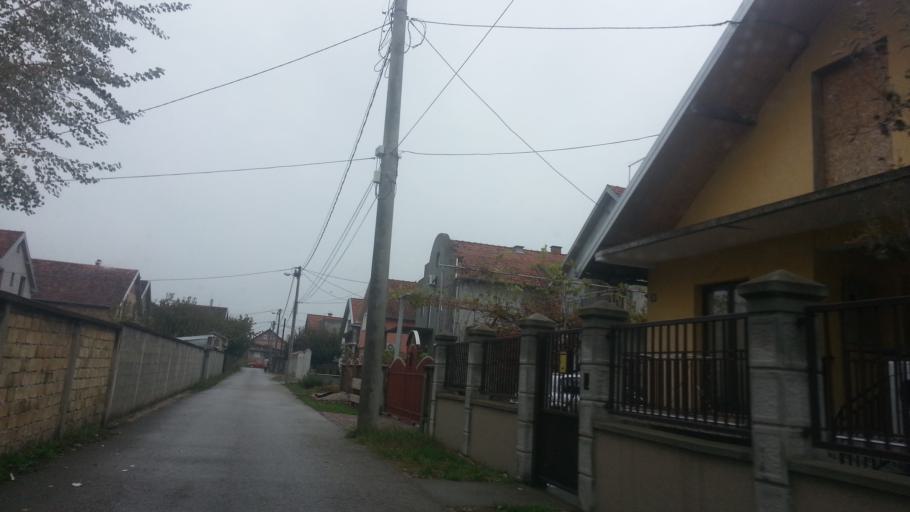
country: RS
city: Novi Banovci
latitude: 44.9042
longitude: 20.2962
